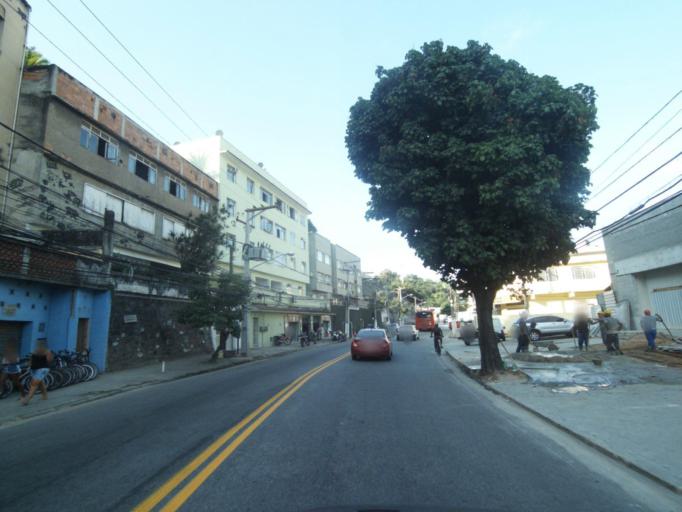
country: BR
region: Rio de Janeiro
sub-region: Niteroi
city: Niteroi
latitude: -22.8908
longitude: -43.0980
